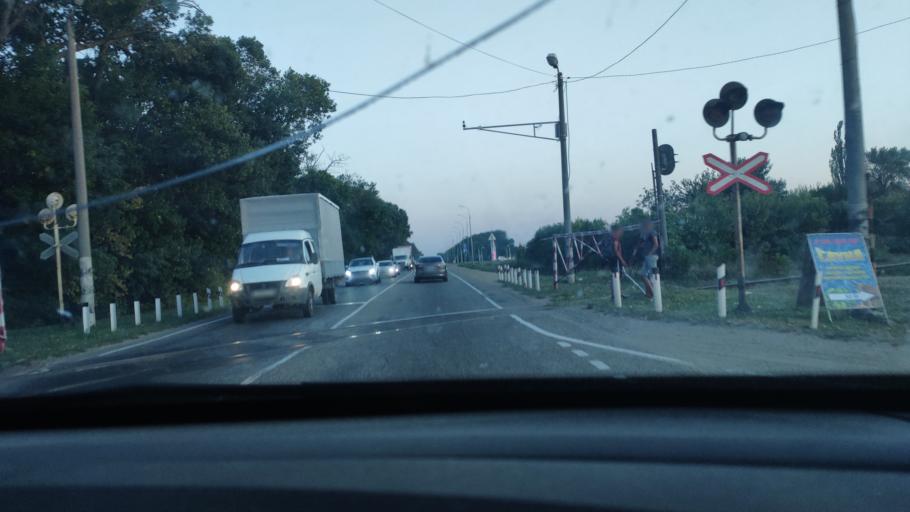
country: RU
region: Krasnodarskiy
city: Medvedovskaya
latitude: 45.4485
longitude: 38.9925
